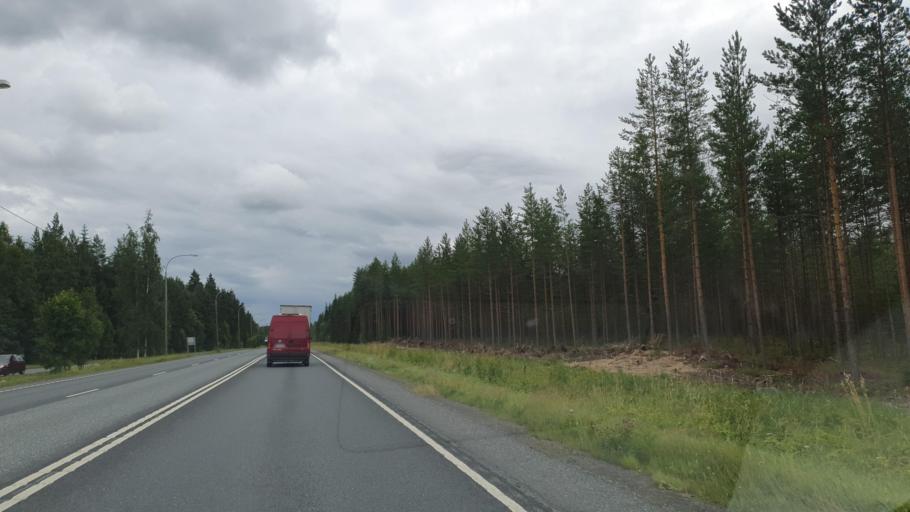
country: FI
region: Northern Savo
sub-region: Ylae-Savo
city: Iisalmi
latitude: 63.4765
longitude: 27.2981
